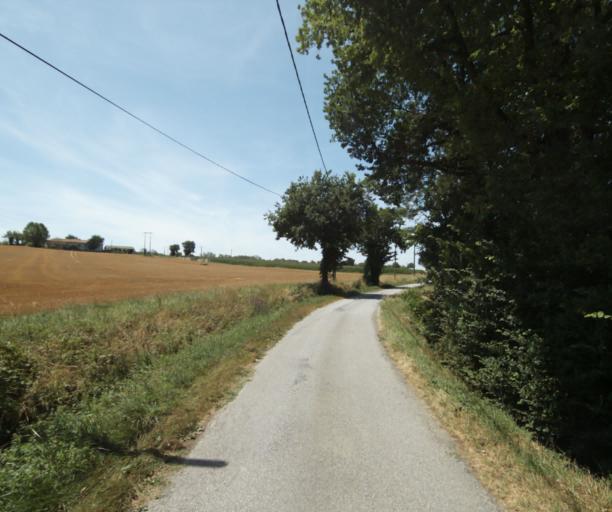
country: FR
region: Midi-Pyrenees
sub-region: Departement du Tarn
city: Soreze
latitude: 43.4908
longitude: 2.0427
